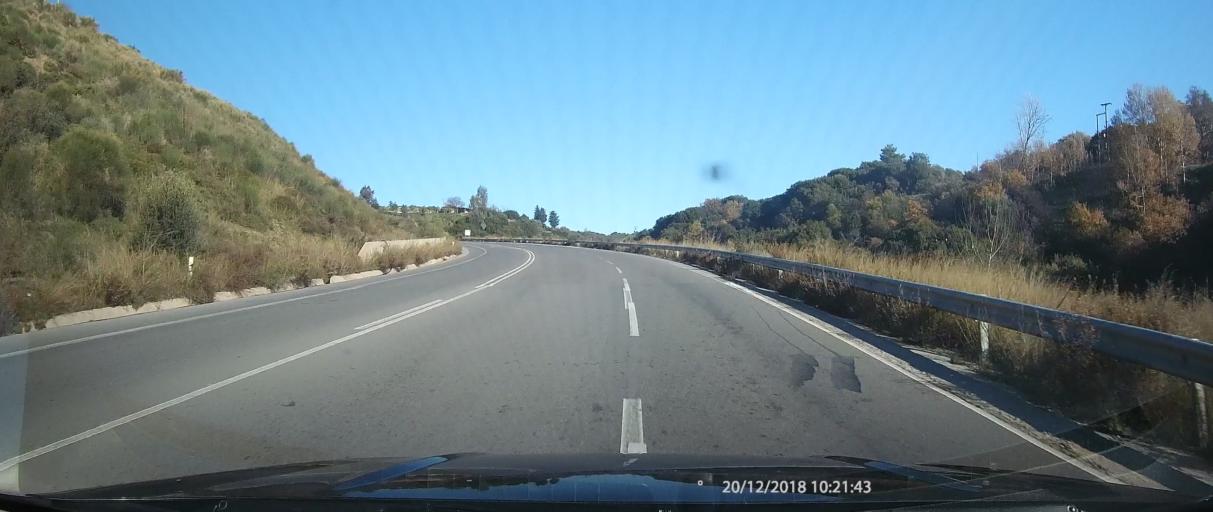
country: GR
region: Peloponnese
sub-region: Nomos Lakonias
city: Magoula
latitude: 37.1641
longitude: 22.4271
